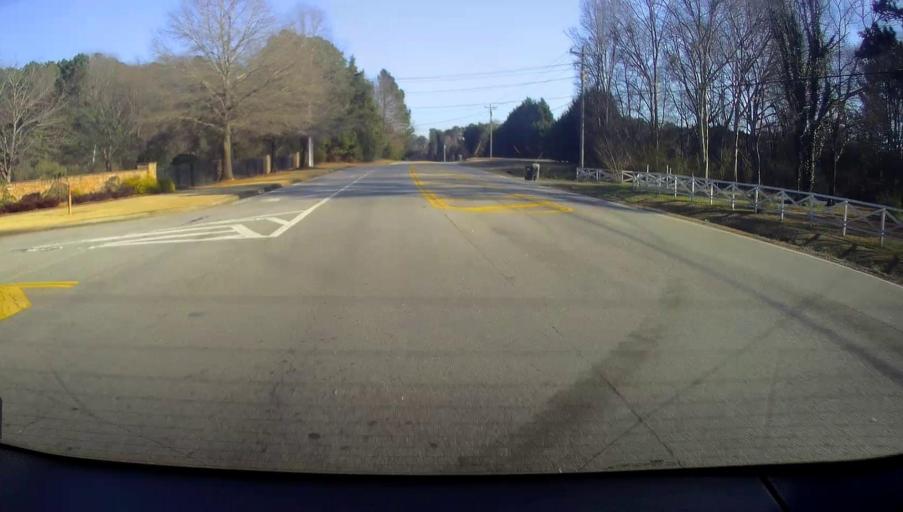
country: US
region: Georgia
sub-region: Henry County
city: Locust Grove
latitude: 33.3560
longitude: -84.1574
